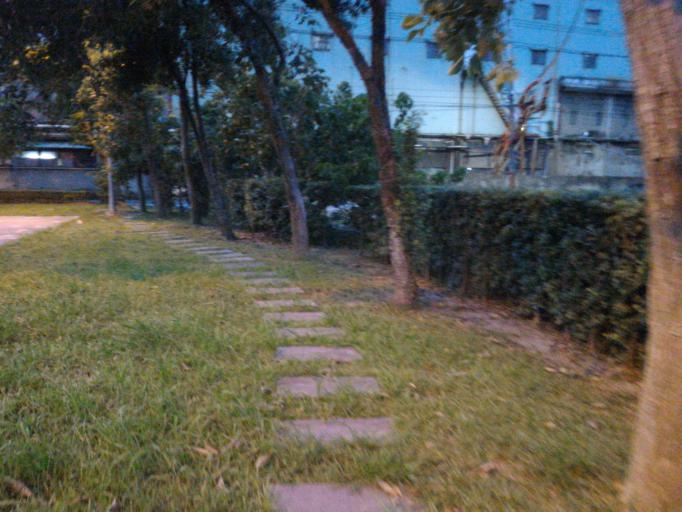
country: TW
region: Taipei
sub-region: Taipei
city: Banqiao
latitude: 24.9615
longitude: 121.4008
